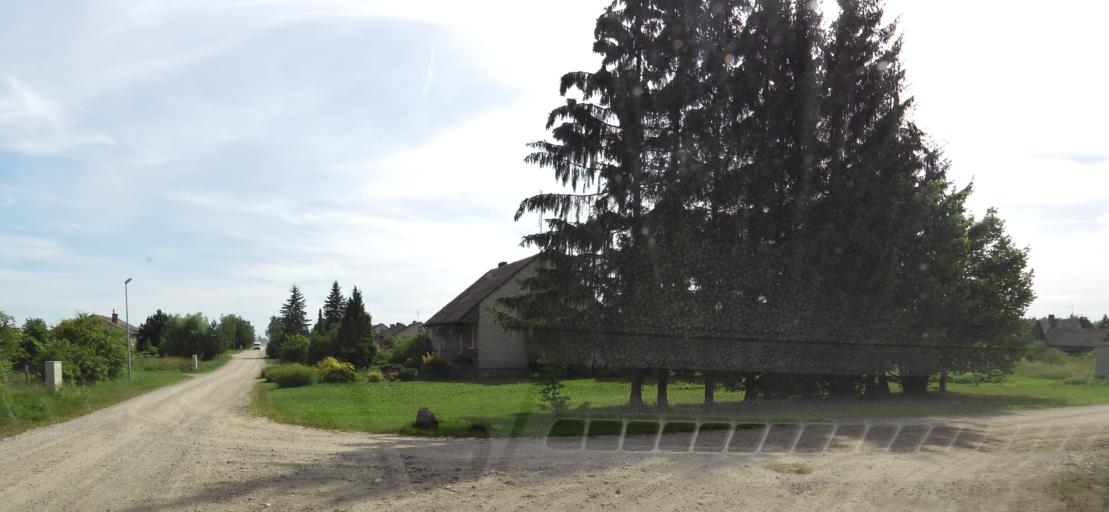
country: LT
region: Panevezys
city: Pasvalys
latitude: 55.9326
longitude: 24.3488
